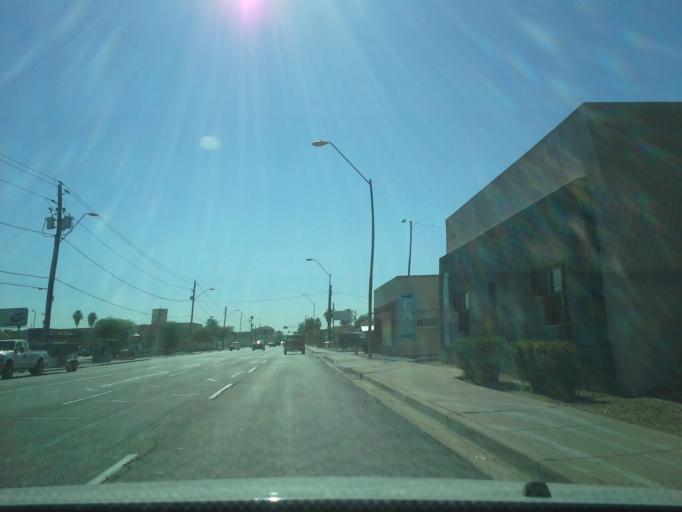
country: US
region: Arizona
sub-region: Maricopa County
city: Phoenix
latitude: 33.4656
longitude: -112.0251
